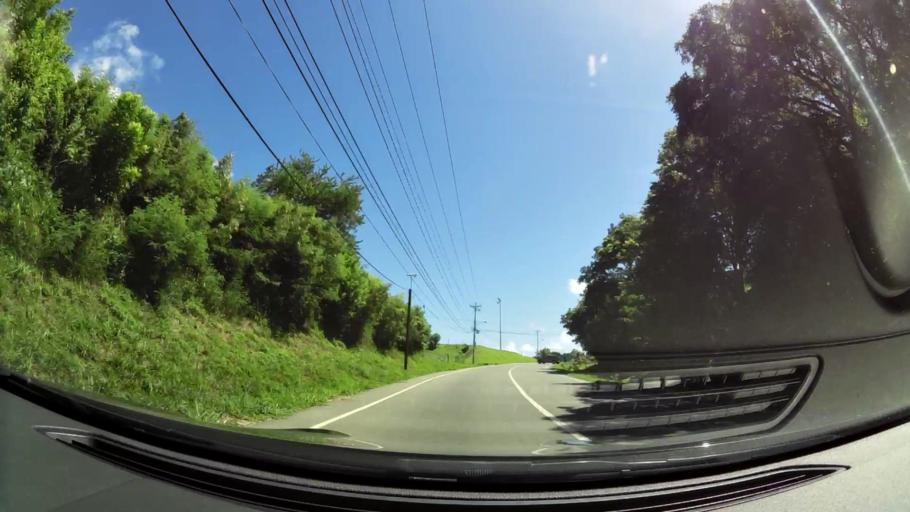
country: TT
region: Tobago
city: Scarborough
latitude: 11.1782
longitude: -60.7896
